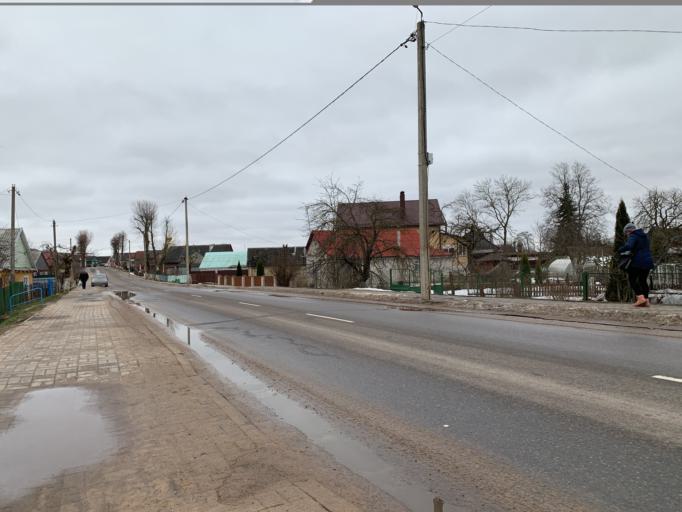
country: BY
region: Minsk
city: Nyasvizh
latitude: 53.2269
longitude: 26.6780
